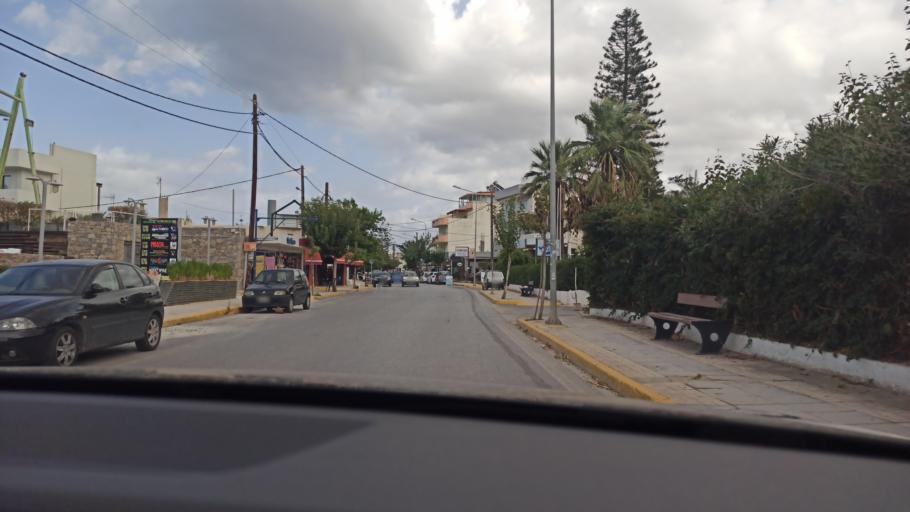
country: GR
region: Crete
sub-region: Nomos Irakleiou
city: Gazi
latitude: 35.3357
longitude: 25.0707
